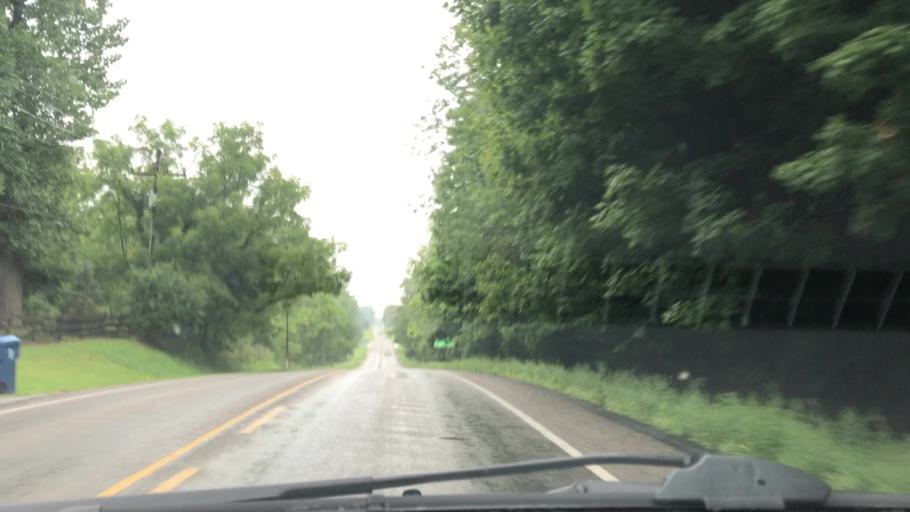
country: US
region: Indiana
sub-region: Hamilton County
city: Westfield
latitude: 40.0968
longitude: -86.1334
